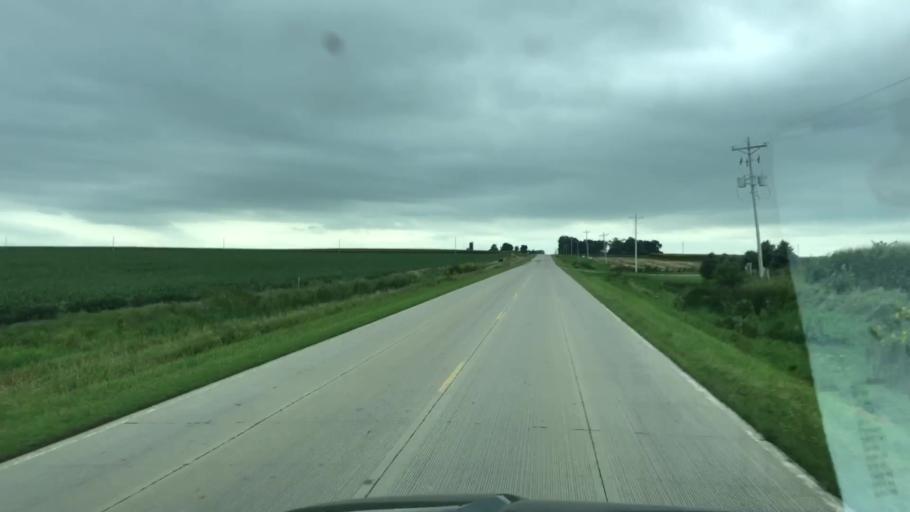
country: US
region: Iowa
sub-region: Sioux County
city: Alton
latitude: 43.1029
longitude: -95.9785
